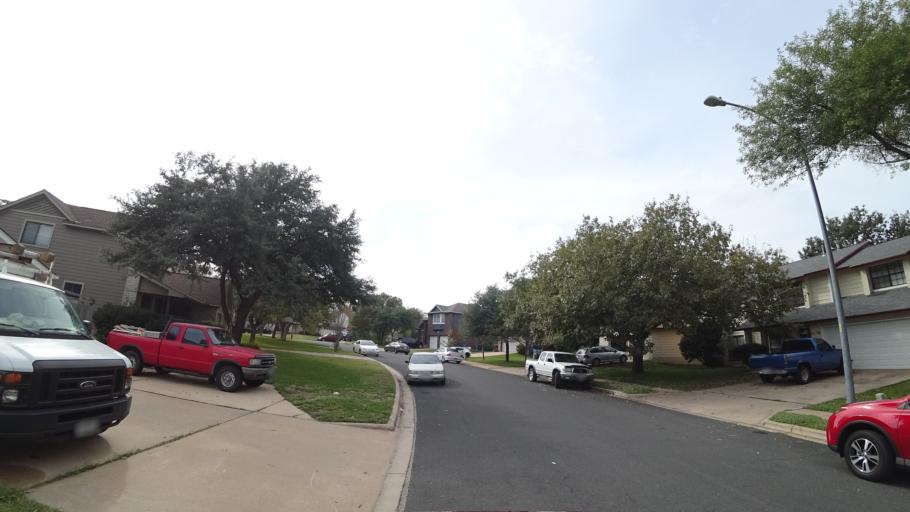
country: US
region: Texas
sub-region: Travis County
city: Wells Branch
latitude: 30.4473
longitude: -97.6831
